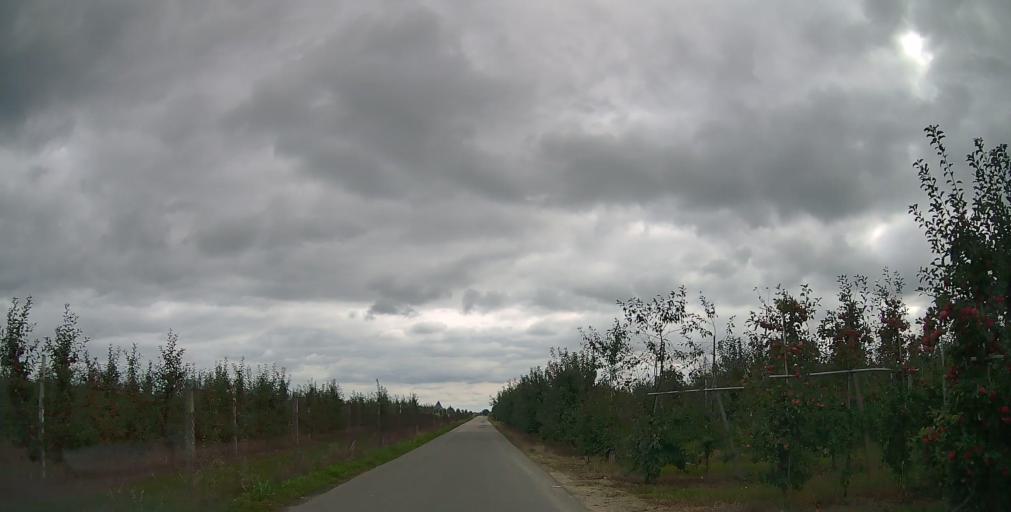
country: PL
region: Masovian Voivodeship
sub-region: Powiat grojecki
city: Goszczyn
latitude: 51.7736
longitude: 20.8640
